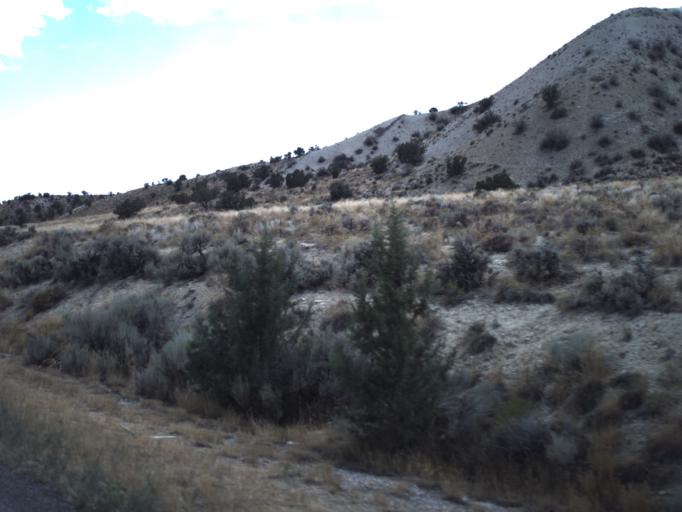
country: US
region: Utah
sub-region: Sanpete County
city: Centerfield
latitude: 39.1369
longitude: -111.7304
